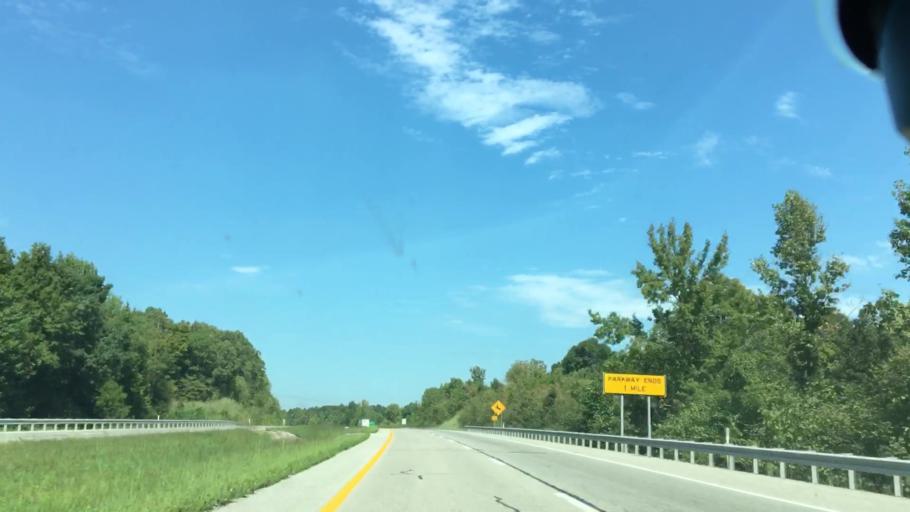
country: US
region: Kentucky
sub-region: Hopkins County
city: Nortonville
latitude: 37.1980
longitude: -87.4397
